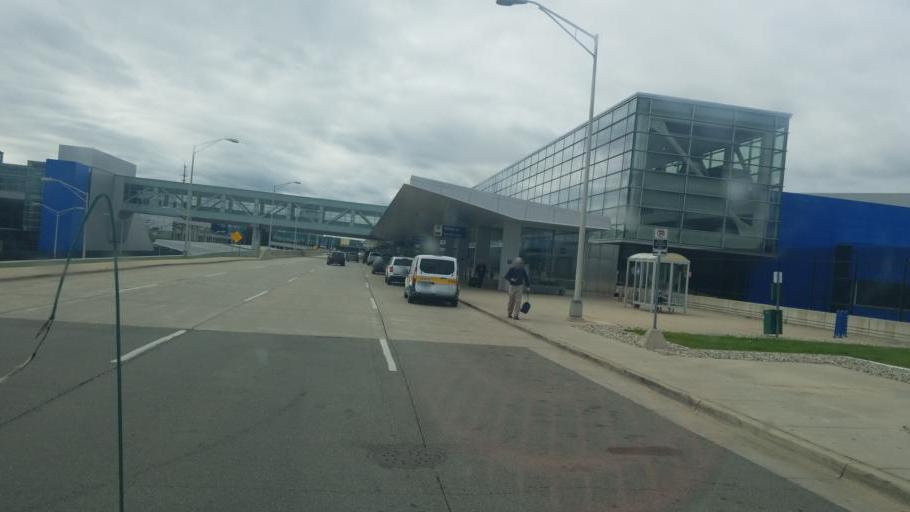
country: US
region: Michigan
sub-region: Wayne County
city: Romulus
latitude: 42.2268
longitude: -83.3468
